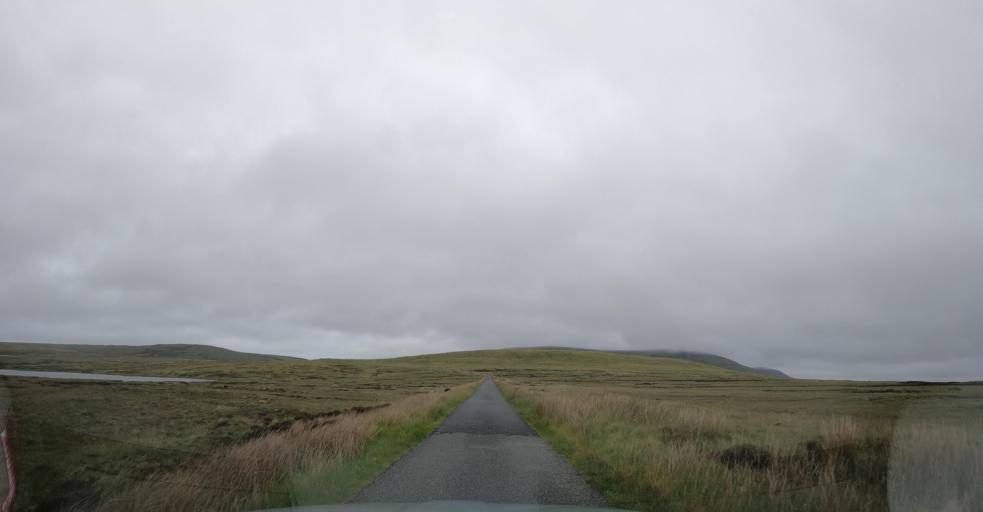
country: GB
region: Scotland
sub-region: Eilean Siar
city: Isle of North Uist
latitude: 57.5918
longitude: -7.3889
